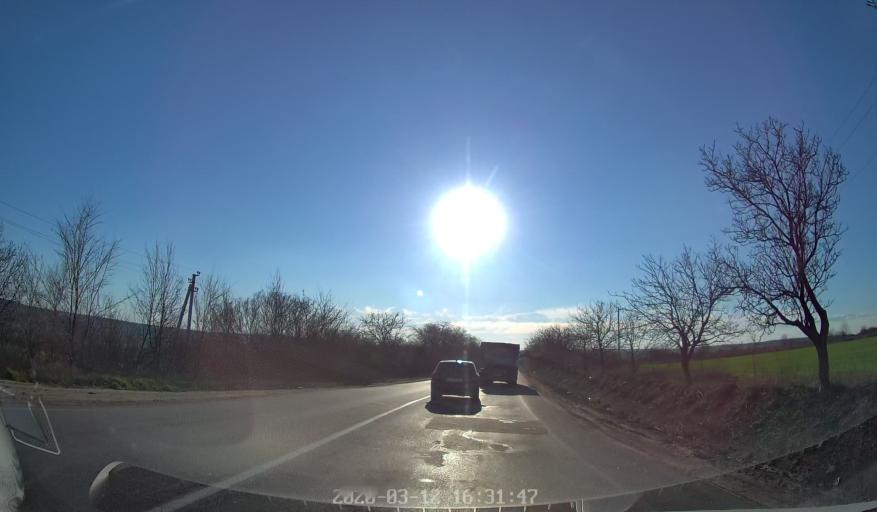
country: MD
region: Anenii Noi
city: Anenii Noi
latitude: 46.8308
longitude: 29.2215
